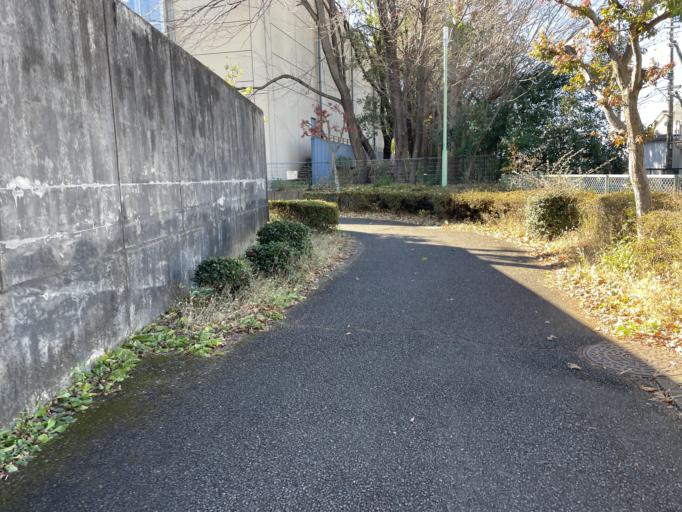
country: JP
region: Saitama
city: Sakado
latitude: 35.9255
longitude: 139.4064
